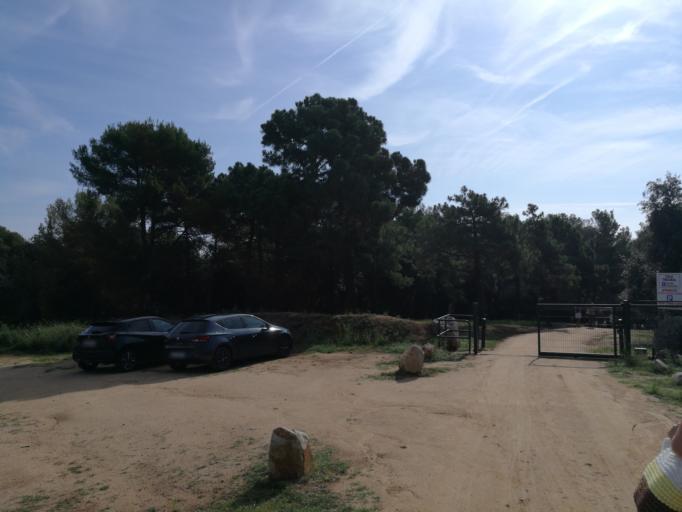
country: ES
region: Catalonia
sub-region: Provincia de Girona
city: Blanes
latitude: 41.6876
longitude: 2.8138
